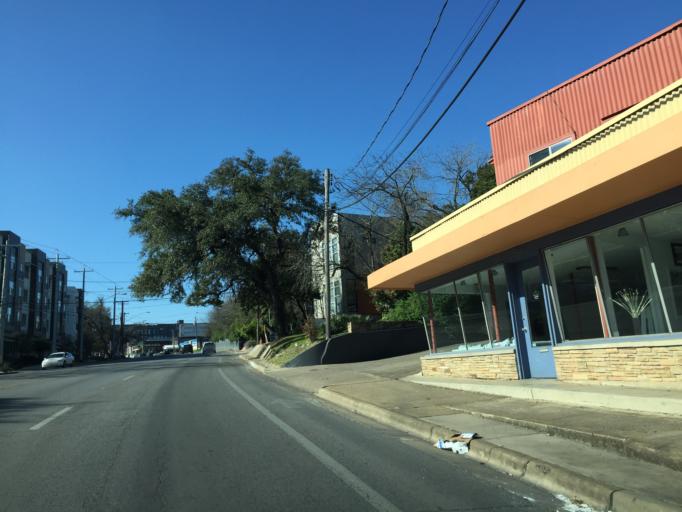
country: US
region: Texas
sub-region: Travis County
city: Austin
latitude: 30.2580
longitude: -97.7597
